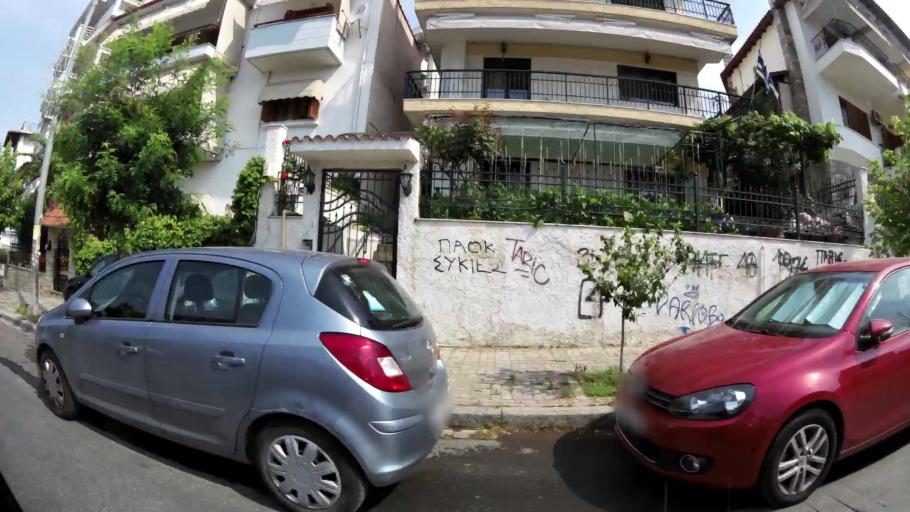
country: GR
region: Central Macedonia
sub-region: Nomos Thessalonikis
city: Agios Pavlos
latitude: 40.6466
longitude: 22.9581
